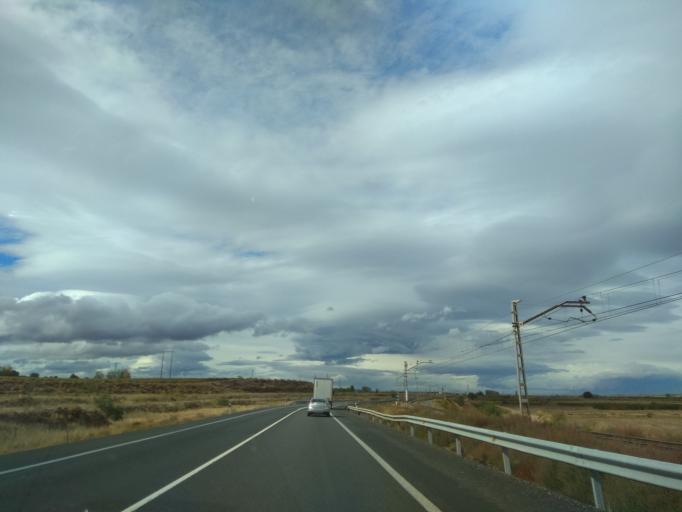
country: ES
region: Navarre
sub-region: Provincia de Navarra
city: Milagro
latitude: 42.2091
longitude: -1.8038
